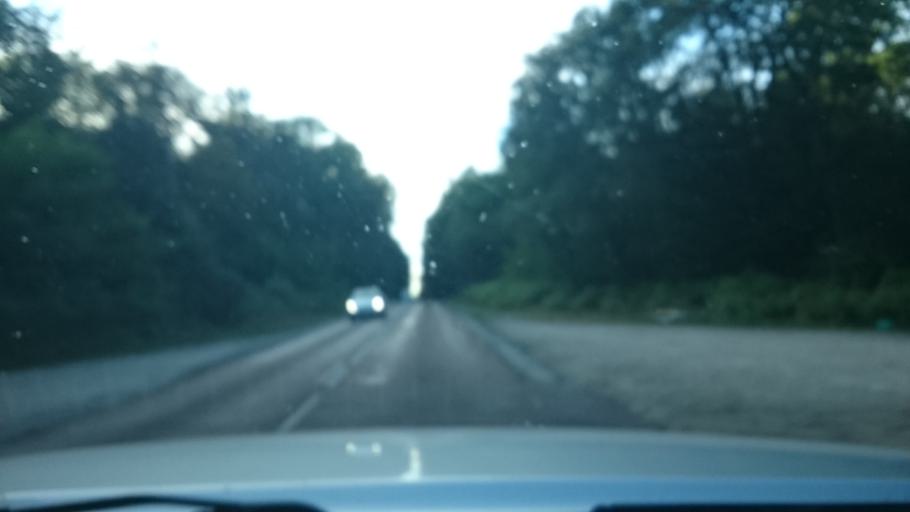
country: FR
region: Ile-de-France
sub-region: Departement de Seine-et-Marne
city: Samoreau
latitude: 48.4019
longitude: 2.7574
